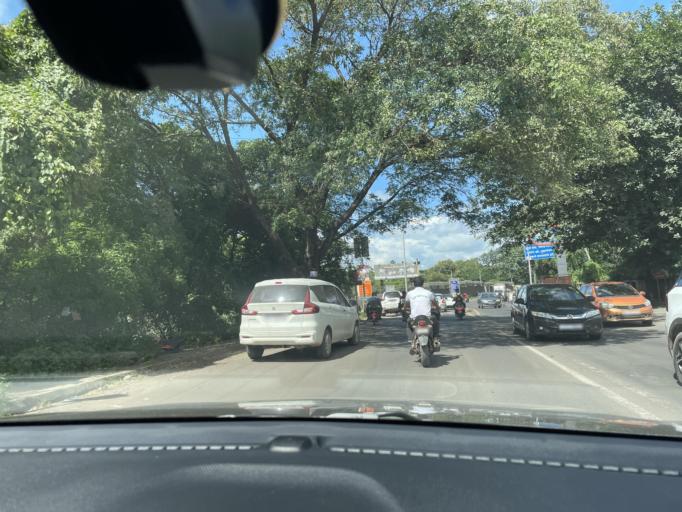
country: IN
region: Maharashtra
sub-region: Pune Division
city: Shivaji Nagar
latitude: 18.5252
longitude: 73.7811
